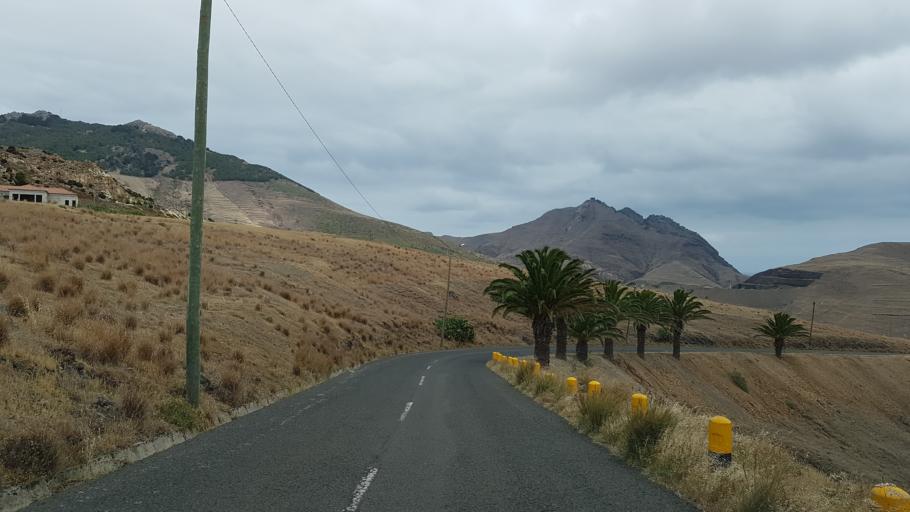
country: PT
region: Madeira
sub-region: Porto Santo
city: Vila de Porto Santo
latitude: 33.0669
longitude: -16.3169
